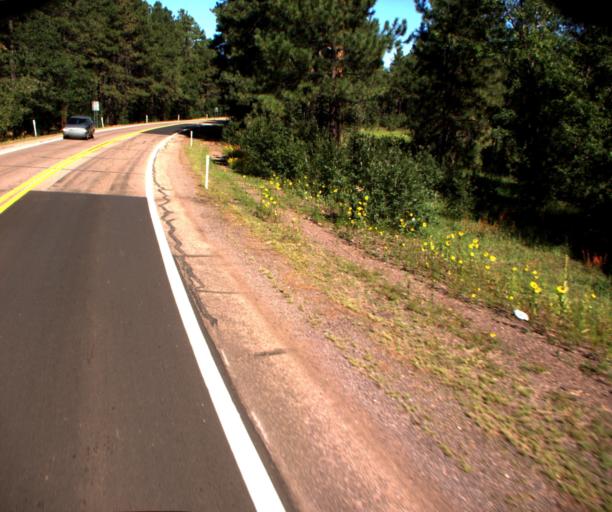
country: US
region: Arizona
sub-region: Navajo County
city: Pinetop-Lakeside
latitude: 34.0743
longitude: -109.8623
